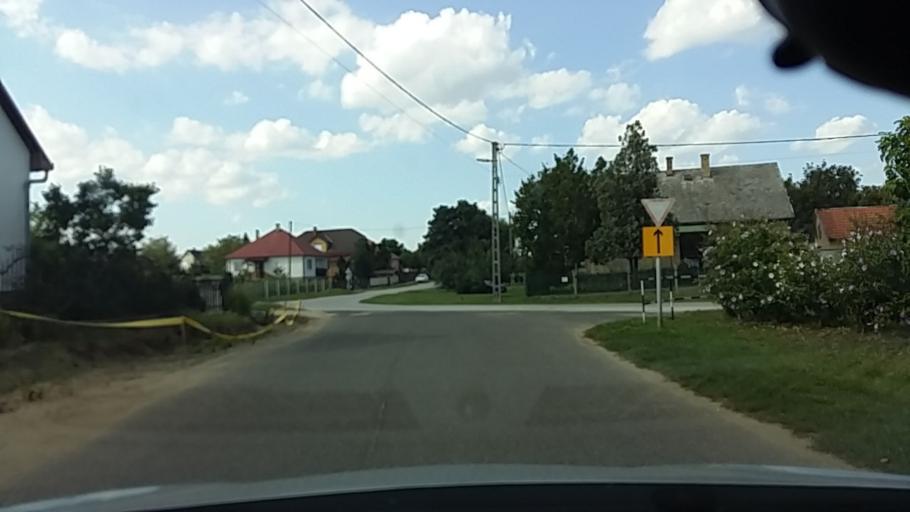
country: HU
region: Szabolcs-Szatmar-Bereg
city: Nyirpazony
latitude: 48.0119
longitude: 21.8340
